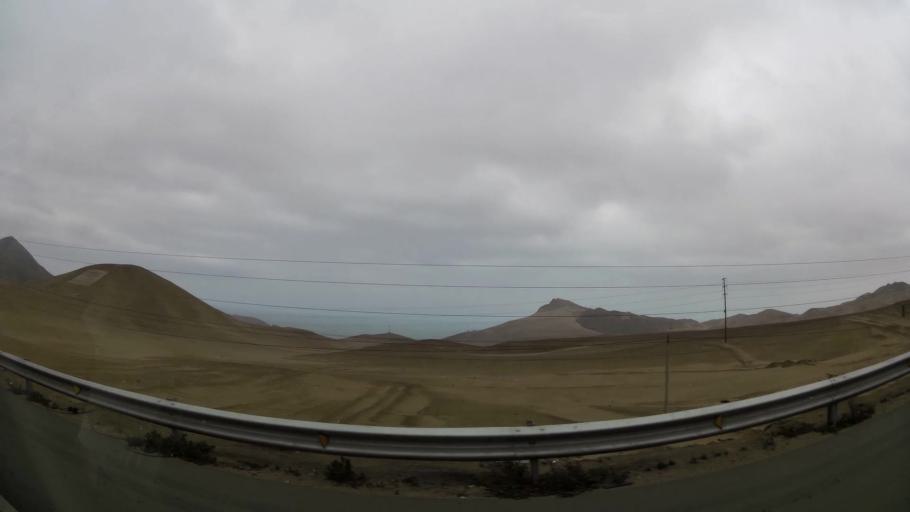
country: PE
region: Lima
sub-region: Lima
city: San Bartolo
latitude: -12.4373
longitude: -76.7556
